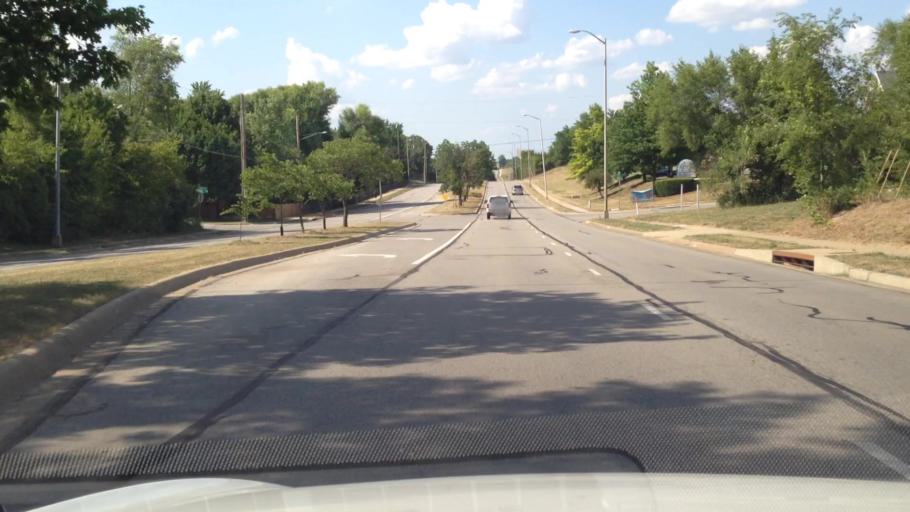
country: US
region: Kansas
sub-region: Johnson County
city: Olathe
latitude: 38.9193
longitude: -94.7973
